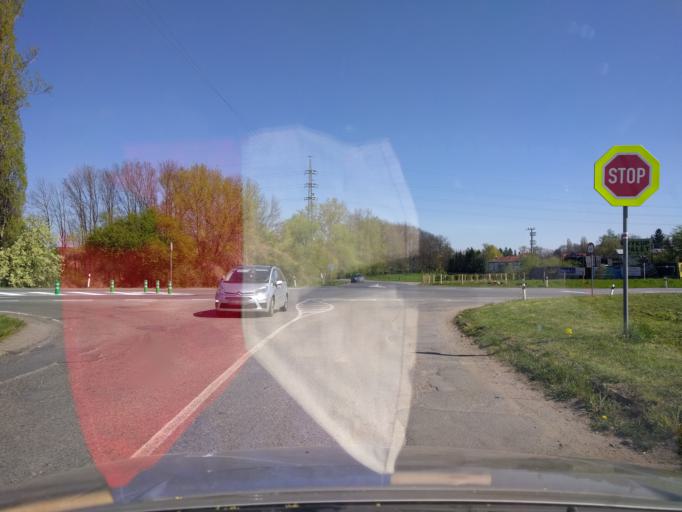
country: CZ
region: Central Bohemia
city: Cesky Brod
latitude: 50.0635
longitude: 14.8479
